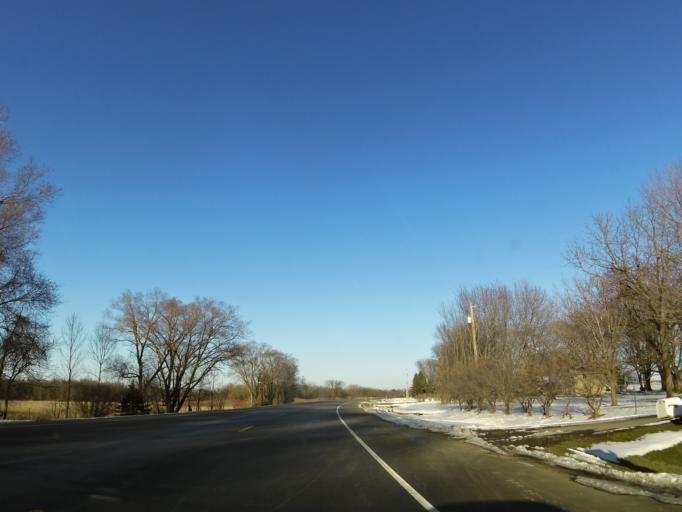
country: US
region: Minnesota
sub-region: Dakota County
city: Farmington
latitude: 44.6573
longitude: -93.1154
